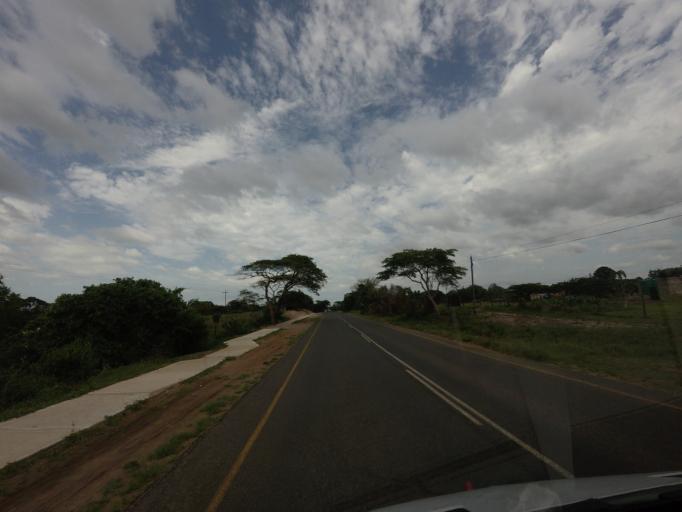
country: ZA
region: KwaZulu-Natal
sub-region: uMkhanyakude District Municipality
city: Mtubatuba
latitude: -28.3784
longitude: 32.3684
